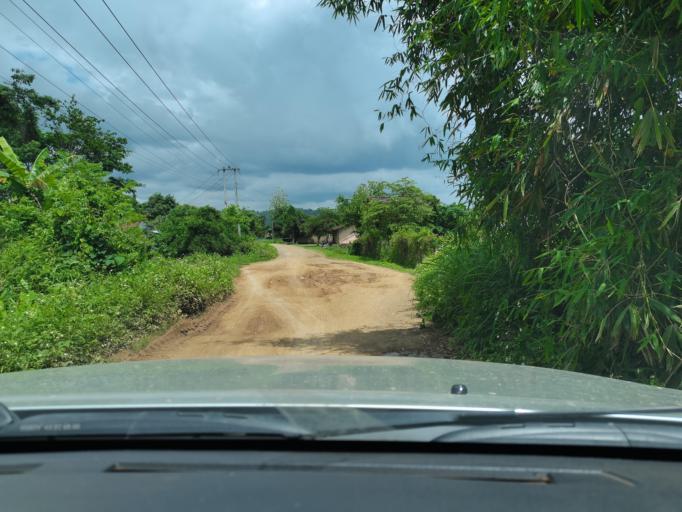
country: LA
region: Loungnamtha
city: Muang Long
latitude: 20.6816
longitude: 101.0523
